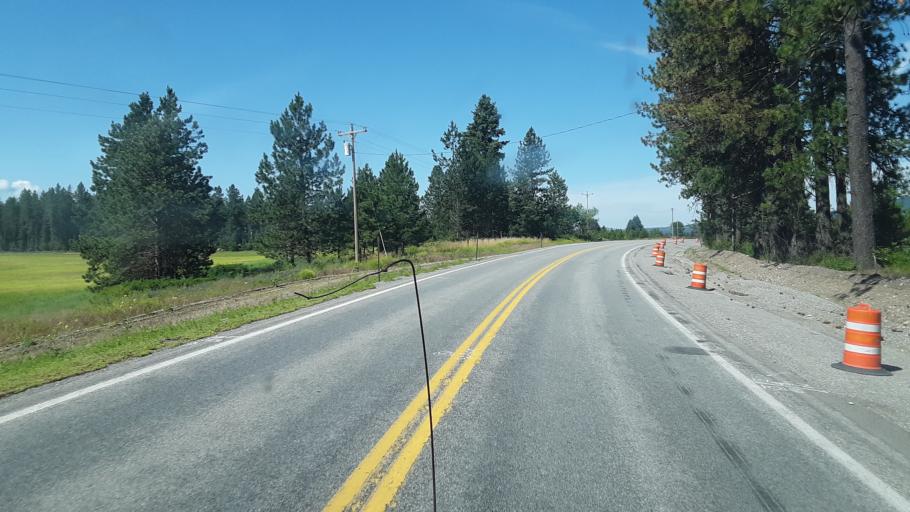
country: US
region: Idaho
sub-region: Kootenai County
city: Hayden
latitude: 47.8177
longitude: -116.7986
